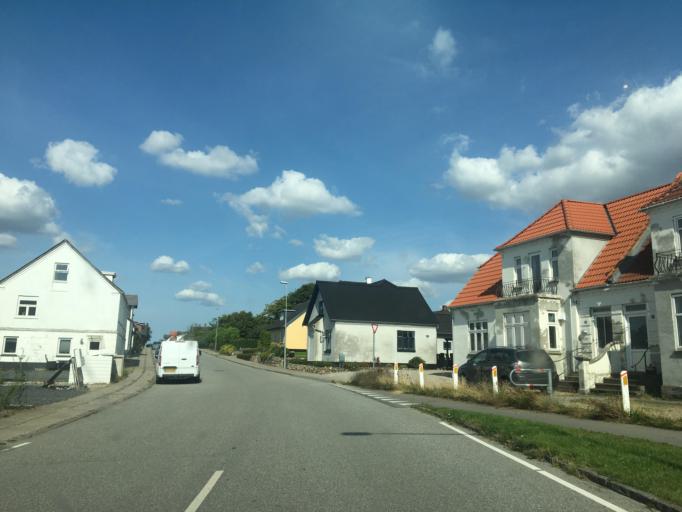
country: DK
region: South Denmark
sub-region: Middelfart Kommune
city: Ejby
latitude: 55.3935
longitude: 9.9673
